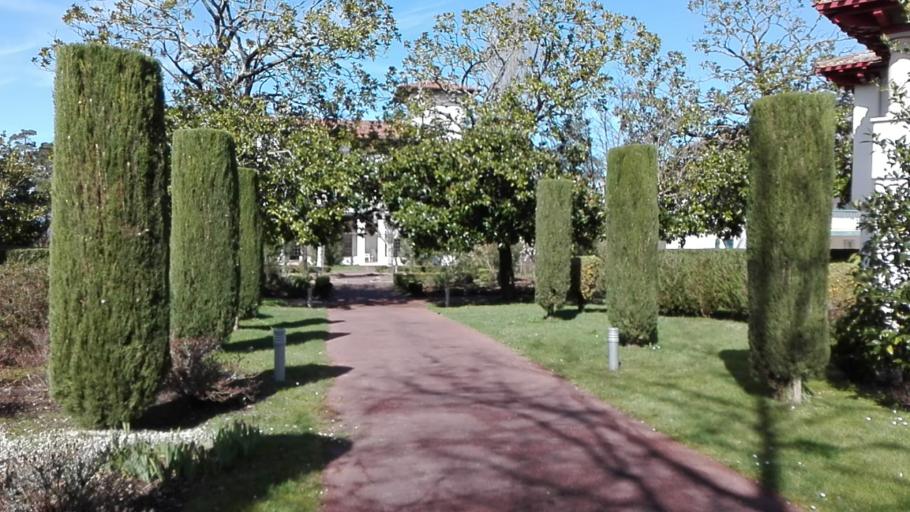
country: FR
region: Aquitaine
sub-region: Departement des Pyrenees-Atlantiques
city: Urrugne
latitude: 43.3765
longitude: -1.7293
